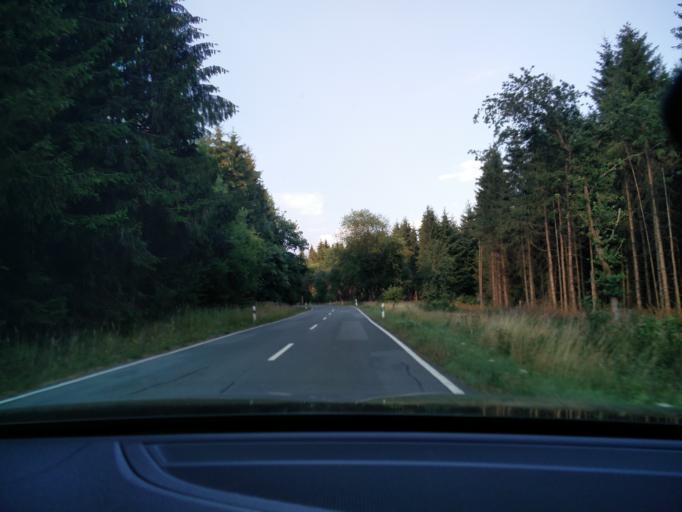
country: DE
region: North Rhine-Westphalia
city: Lichtenau
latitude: 51.6677
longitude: 8.9602
